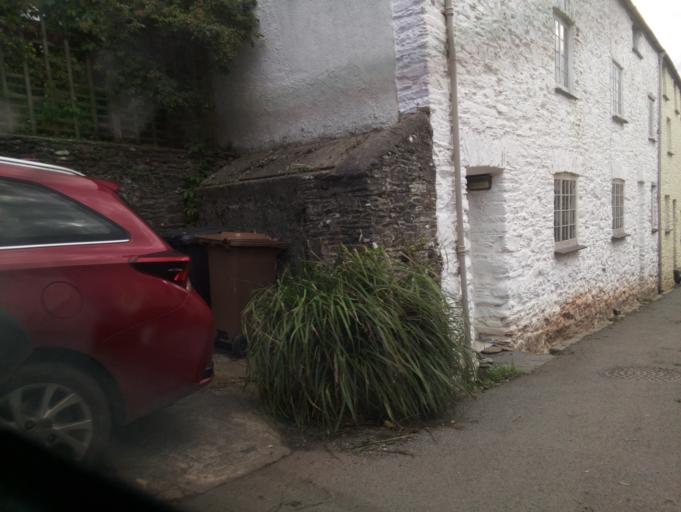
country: GB
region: England
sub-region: Devon
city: Totnes
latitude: 50.3940
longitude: -3.7114
